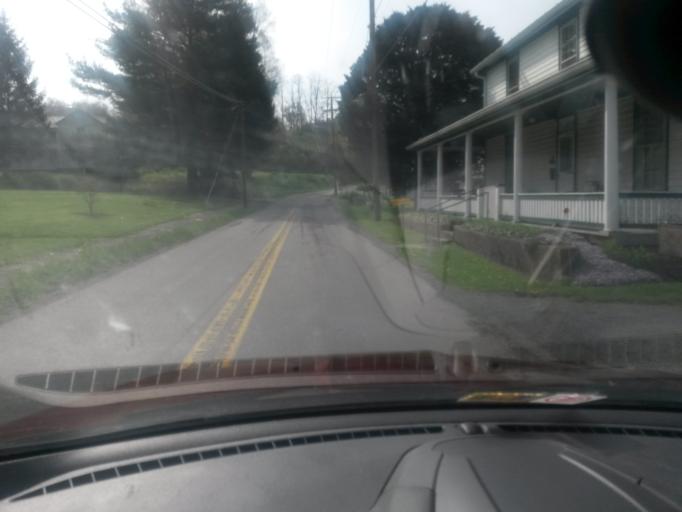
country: US
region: West Virginia
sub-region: Pocahontas County
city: Marlinton
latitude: 38.1343
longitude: -80.2115
